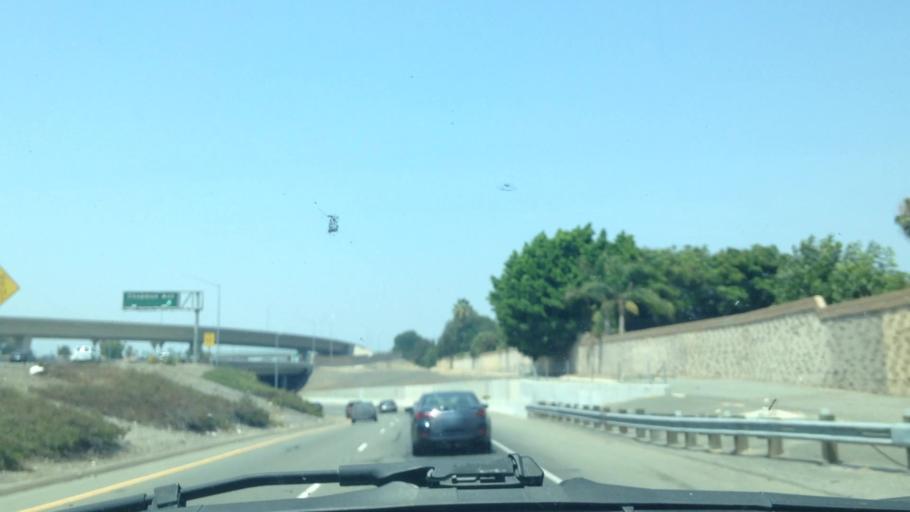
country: US
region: California
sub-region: Orange County
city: Orange
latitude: 33.7747
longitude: -117.8305
